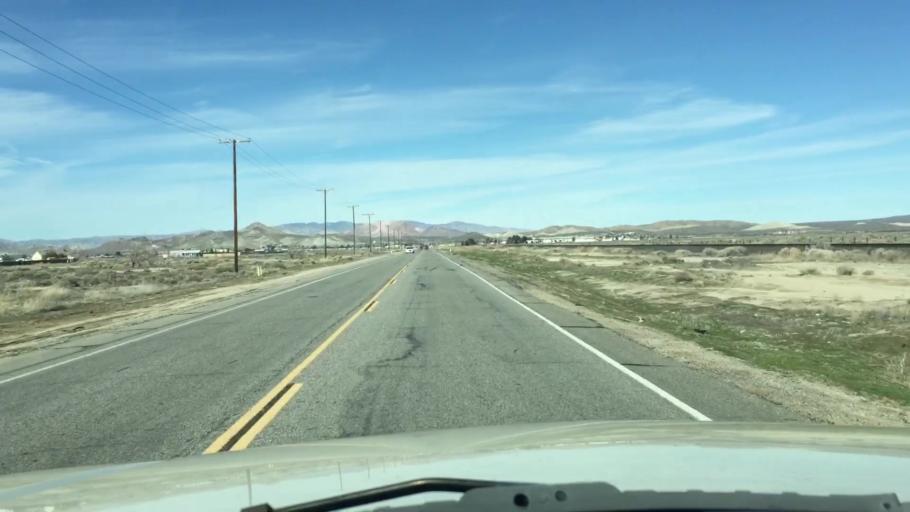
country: US
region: California
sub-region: Kern County
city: Rosamond
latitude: 34.8213
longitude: -118.1562
